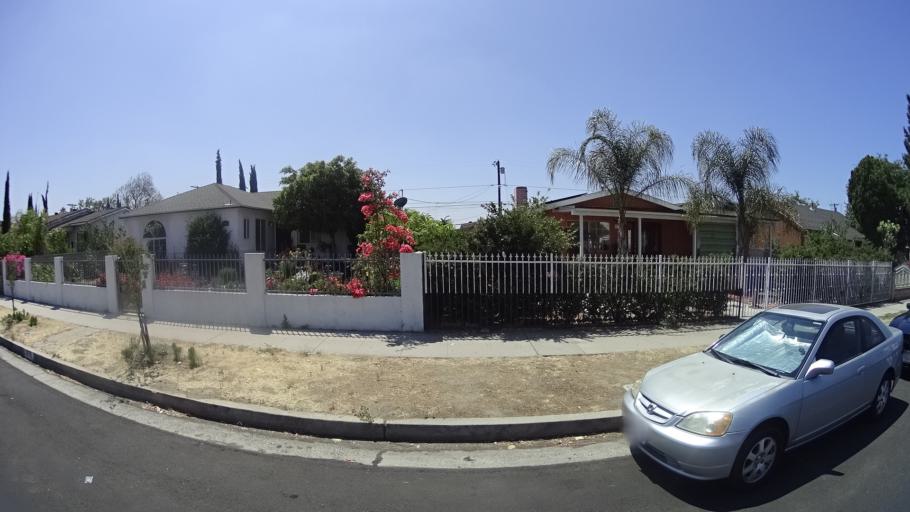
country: US
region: California
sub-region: Los Angeles County
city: San Fernando
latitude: 34.2347
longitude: -118.4361
